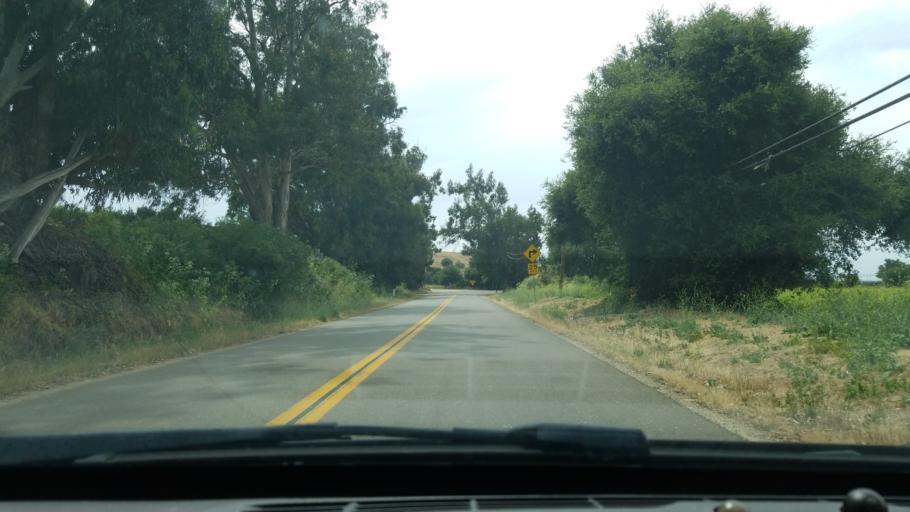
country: US
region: California
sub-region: Santa Barbara County
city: Los Alamos
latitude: 34.8584
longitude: -120.2752
